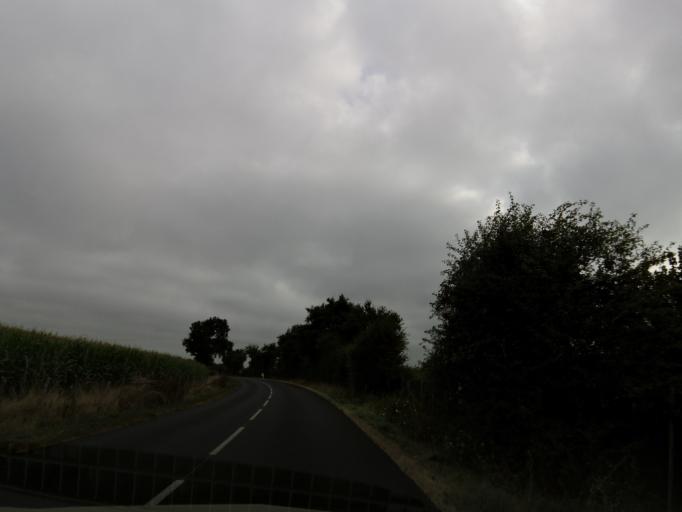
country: FR
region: Pays de la Loire
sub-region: Departement de la Vendee
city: Avrille
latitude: 46.4722
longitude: -1.4488
